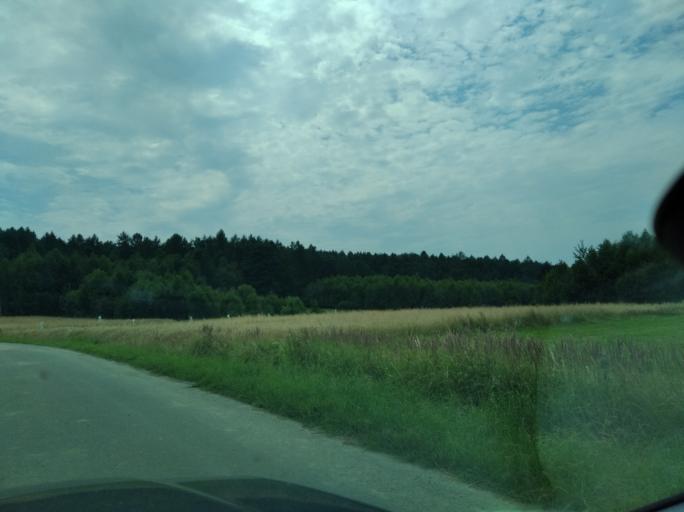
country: PL
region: Subcarpathian Voivodeship
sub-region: Powiat przeworski
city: Lopuszka Wielka
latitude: 49.9115
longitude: 22.3965
